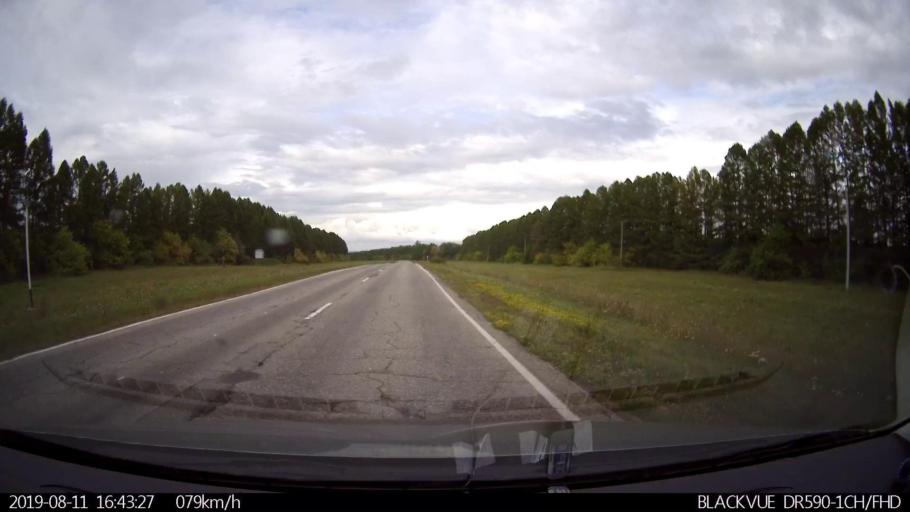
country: RU
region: Ulyanovsk
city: Mayna
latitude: 54.1693
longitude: 47.6724
